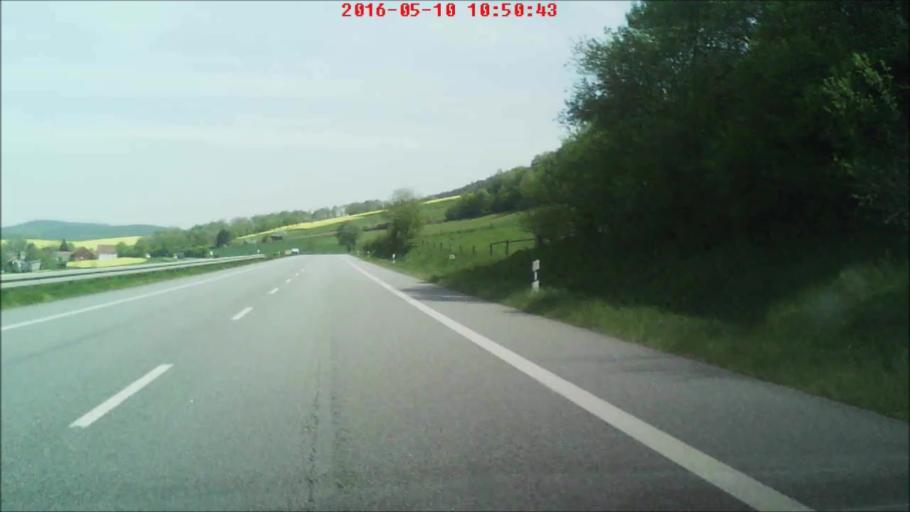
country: DE
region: Hesse
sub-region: Regierungsbezirk Kassel
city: Burghaun
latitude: 50.7790
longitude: 9.7063
